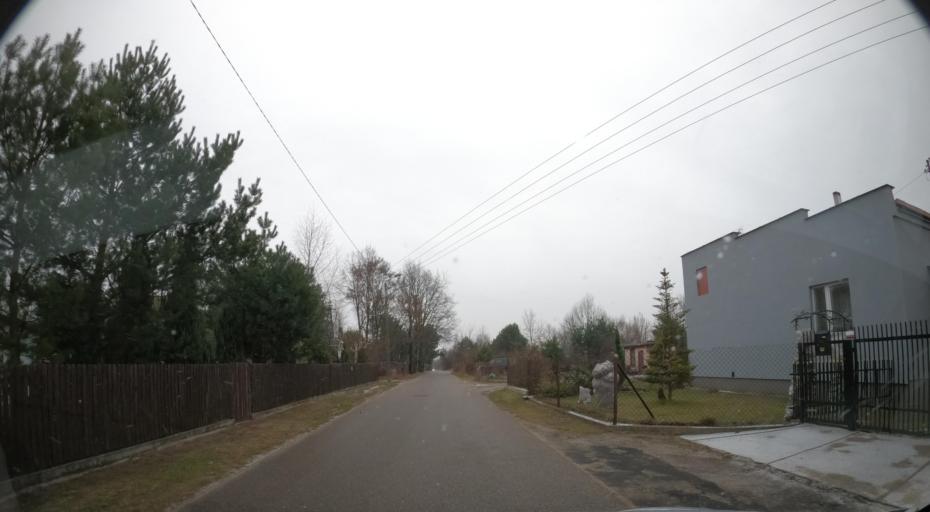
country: PL
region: Masovian Voivodeship
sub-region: Powiat radomski
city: Jastrzebia
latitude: 51.4331
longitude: 21.2287
